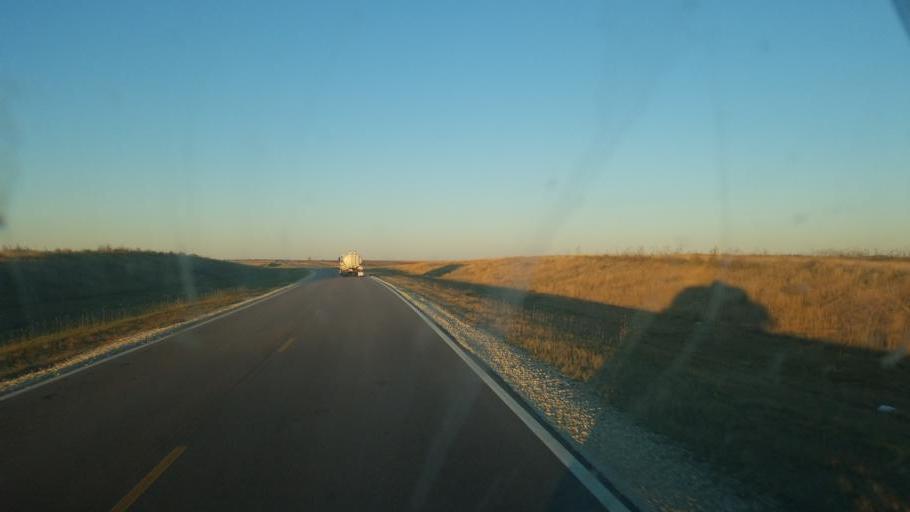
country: US
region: Kansas
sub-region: Wallace County
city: Sharon Springs
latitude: 38.8864
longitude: -101.8942
